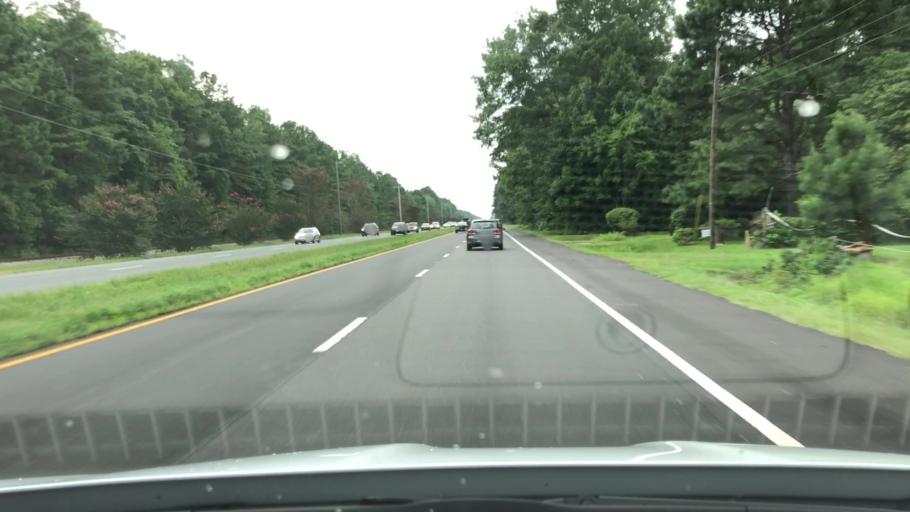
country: US
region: Virginia
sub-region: Northampton County
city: Exmore
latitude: 37.4948
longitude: -75.8455
